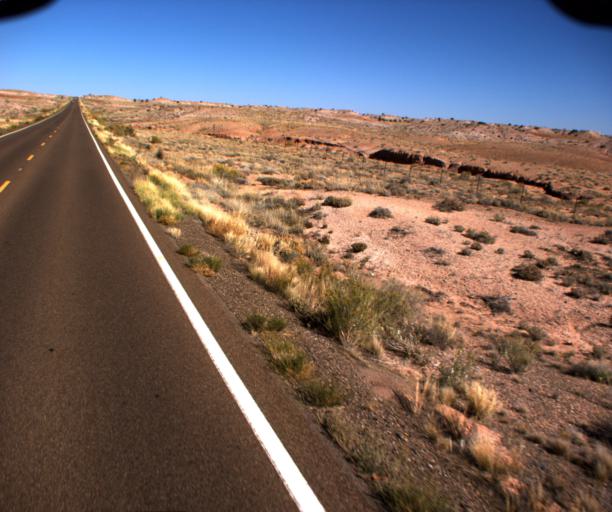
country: US
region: Arizona
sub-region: Navajo County
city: Dilkon
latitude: 35.1982
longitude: -110.4405
